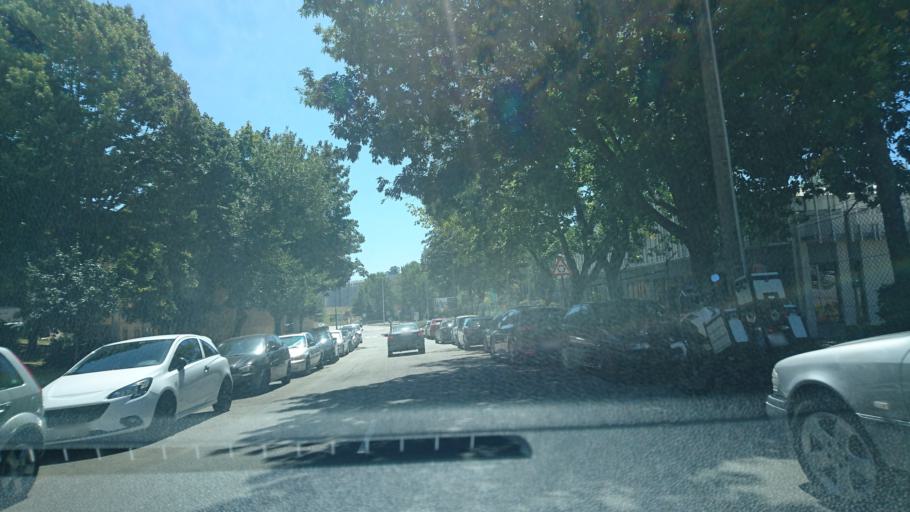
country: PT
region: Porto
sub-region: Gondomar
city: Rio Tinto
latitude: 41.1599
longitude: -8.5709
